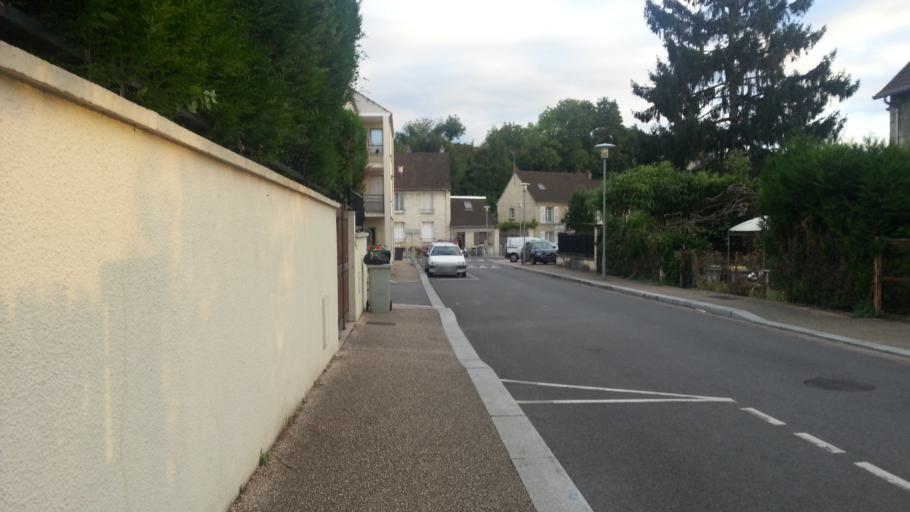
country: FR
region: Picardie
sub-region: Departement de l'Oise
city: Saint-Maximin
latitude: 49.2237
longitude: 2.4413
